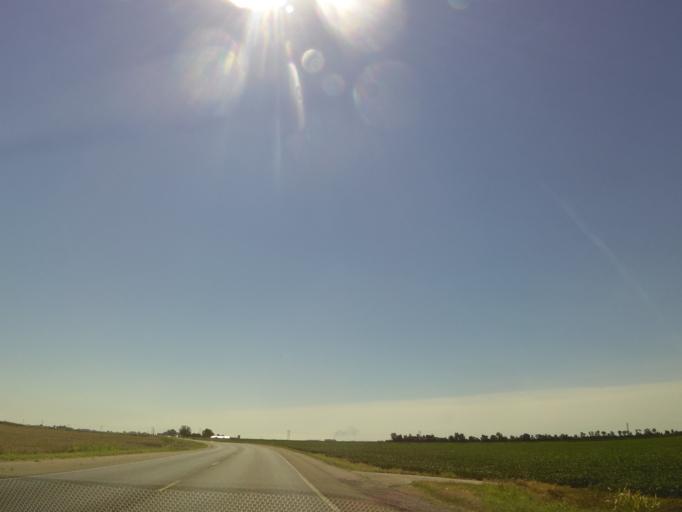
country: US
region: Missouri
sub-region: Dunklin County
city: Malden
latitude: 36.5564
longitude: -89.9540
